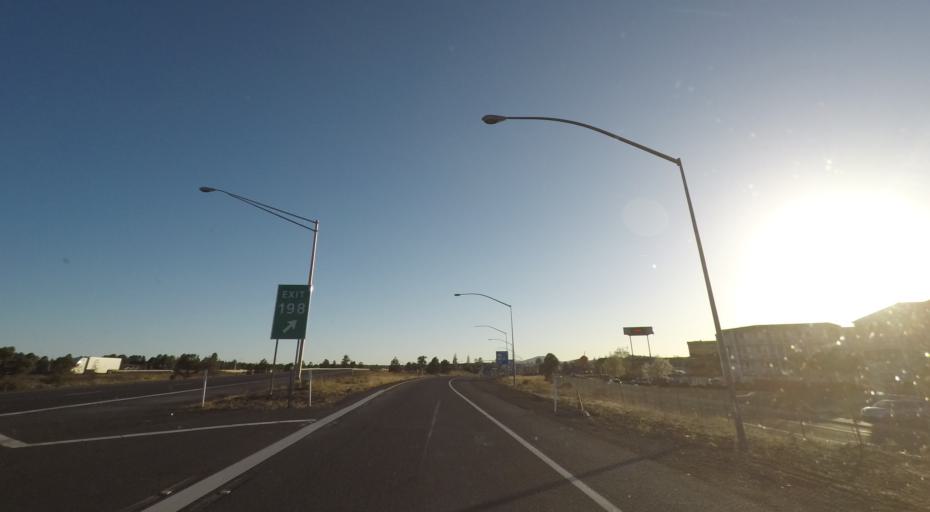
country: US
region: Arizona
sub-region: Coconino County
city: Flagstaff
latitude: 35.1940
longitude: -111.6194
